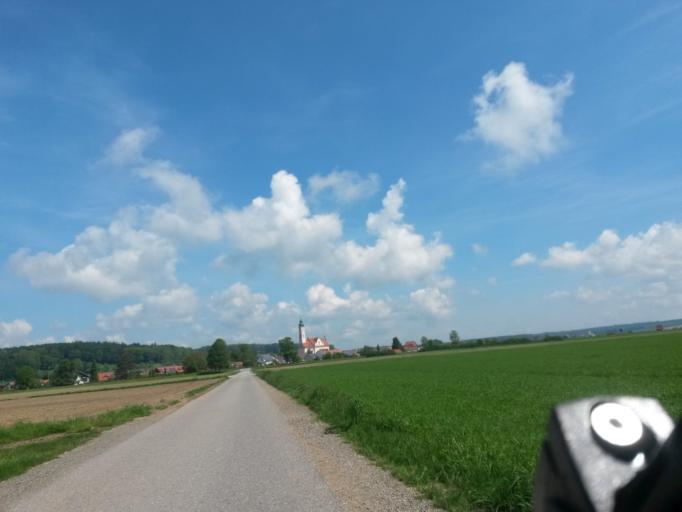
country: DE
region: Baden-Wuerttemberg
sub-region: Tuebingen Region
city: Bad Schussenried
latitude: 48.0221
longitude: 9.6933
